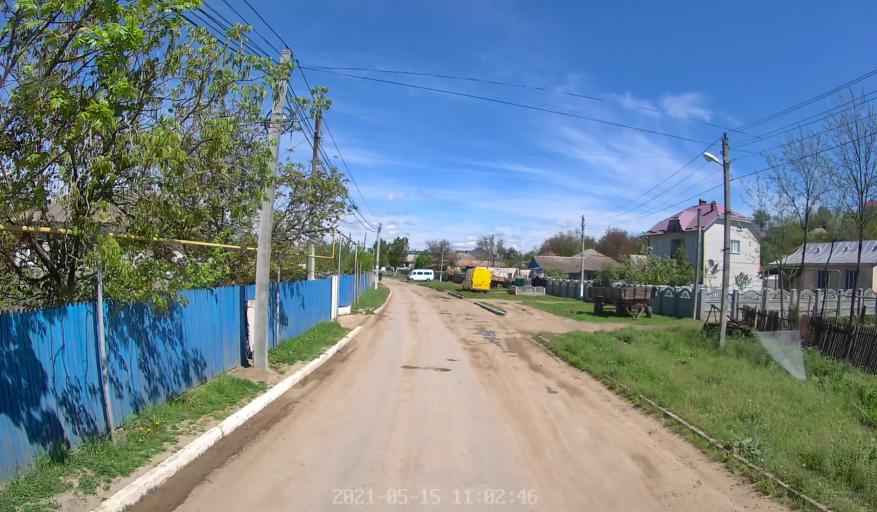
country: MD
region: Hincesti
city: Hincesti
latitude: 46.8302
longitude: 28.6765
